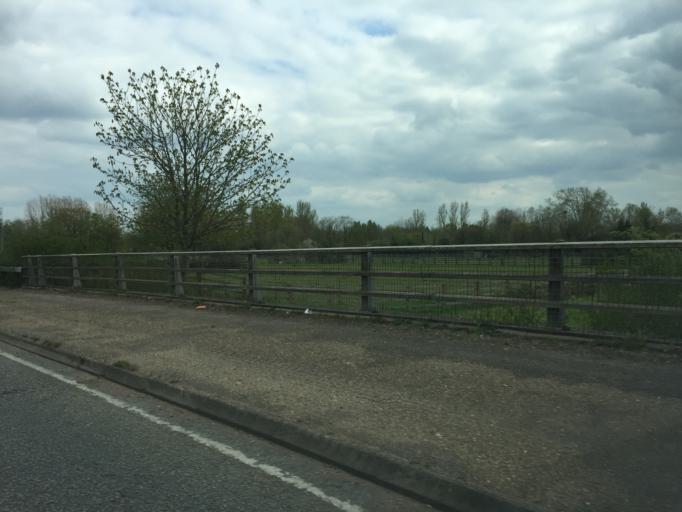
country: GB
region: England
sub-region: Milton Keynes
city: Milton Keynes
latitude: 52.0365
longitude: -0.7284
